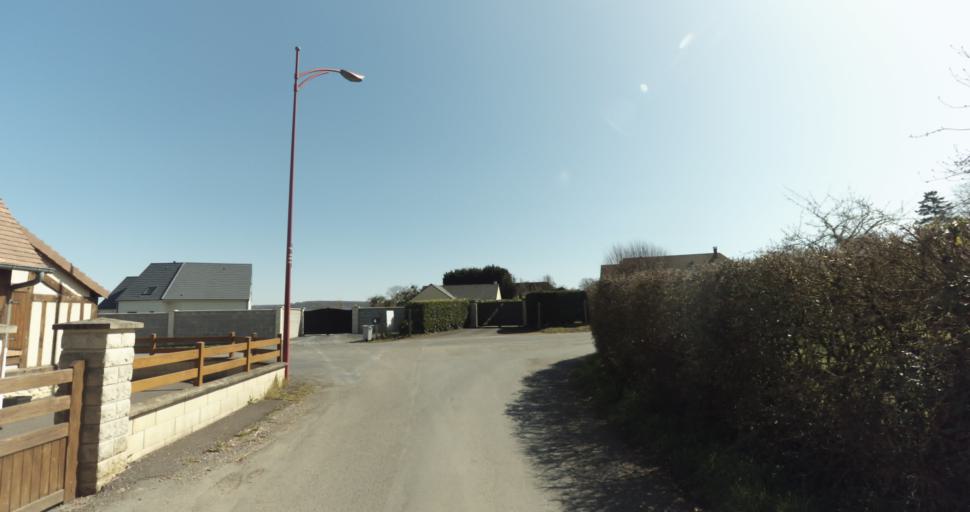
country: FR
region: Lower Normandy
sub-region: Departement du Calvados
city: Saint-Pierre-sur-Dives
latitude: 49.0179
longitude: -0.0062
